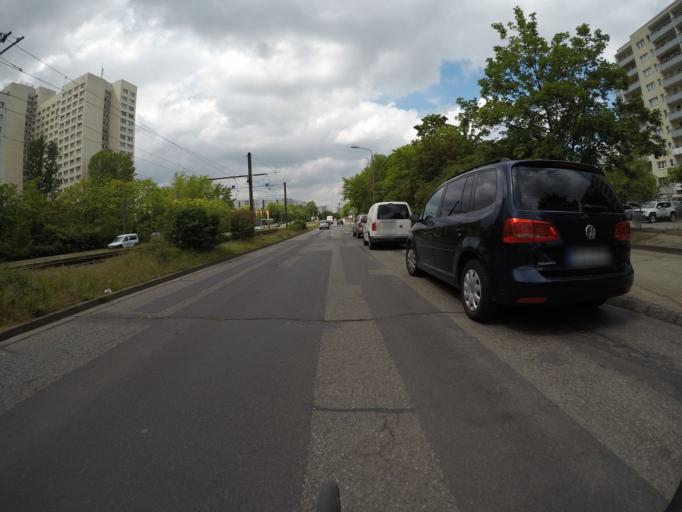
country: DE
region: Berlin
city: Marzahn
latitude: 52.5477
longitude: 13.5602
